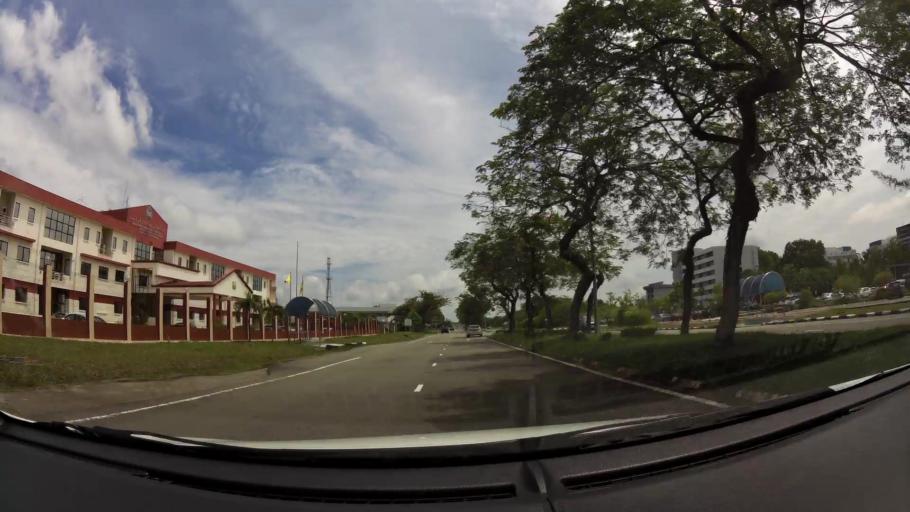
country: BN
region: Brunei and Muara
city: Bandar Seri Begawan
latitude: 4.9247
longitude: 114.9318
